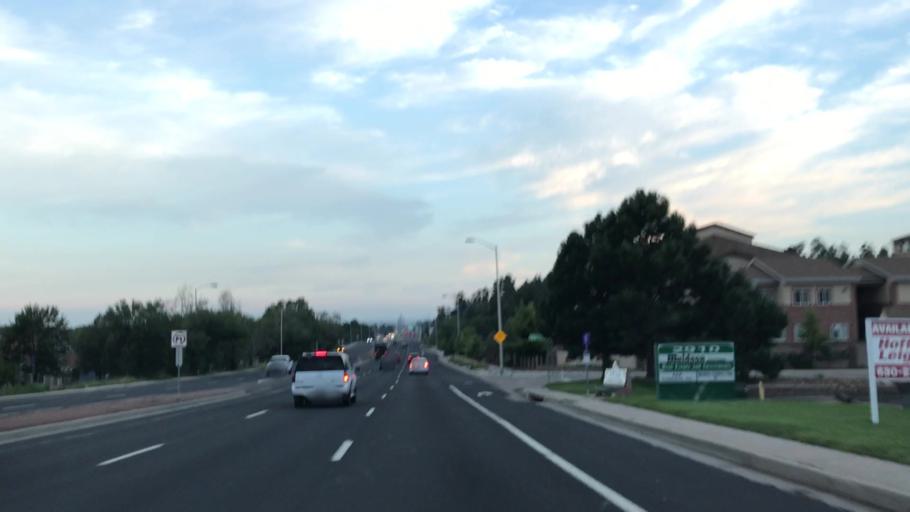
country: US
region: Colorado
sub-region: El Paso County
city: Cimarron Hills
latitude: 38.8743
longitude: -104.7572
